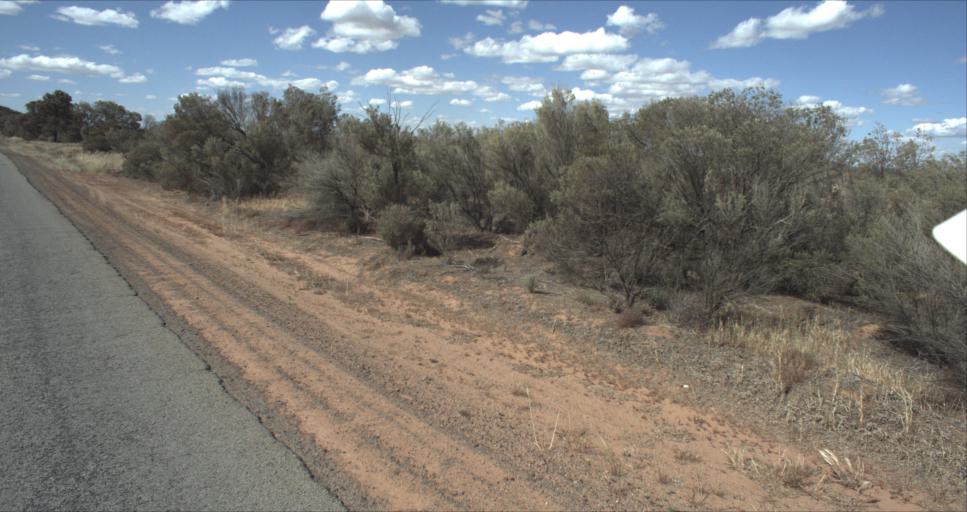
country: AU
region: New South Wales
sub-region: Leeton
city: Leeton
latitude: -34.4785
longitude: 146.2495
